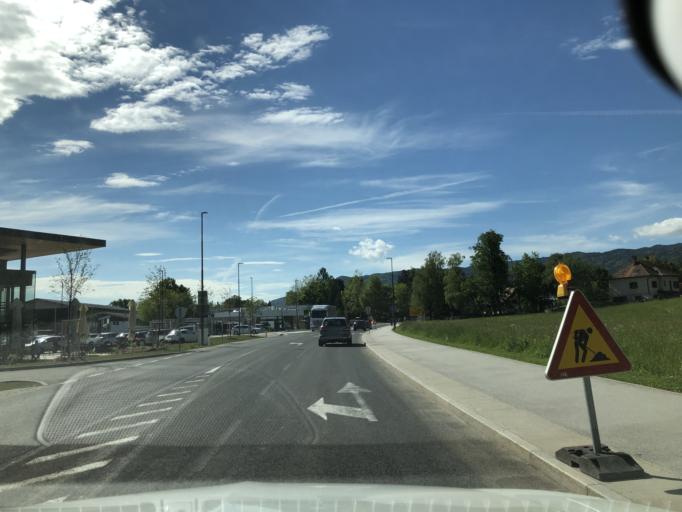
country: SI
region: Bled
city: Bled
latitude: 46.3711
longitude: 14.1153
